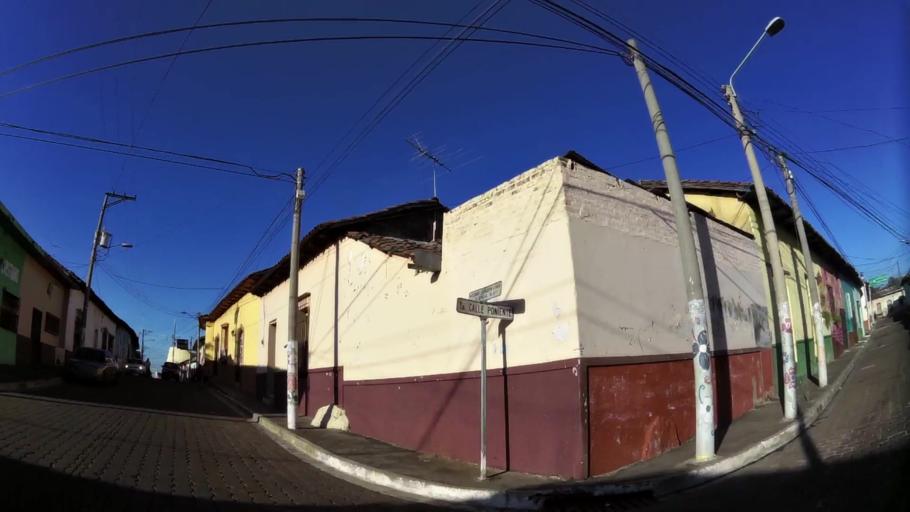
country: SV
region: Sonsonate
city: Sonsonate
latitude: 13.7237
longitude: -89.7263
